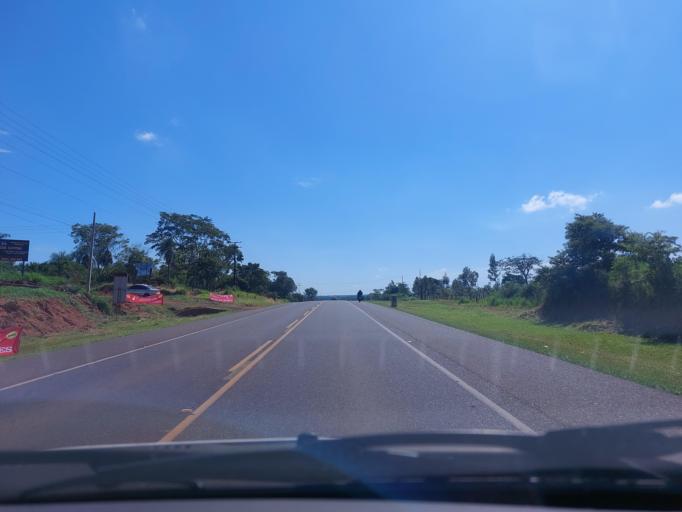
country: PY
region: San Pedro
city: Guayaybi
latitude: -24.6204
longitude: -56.4793
